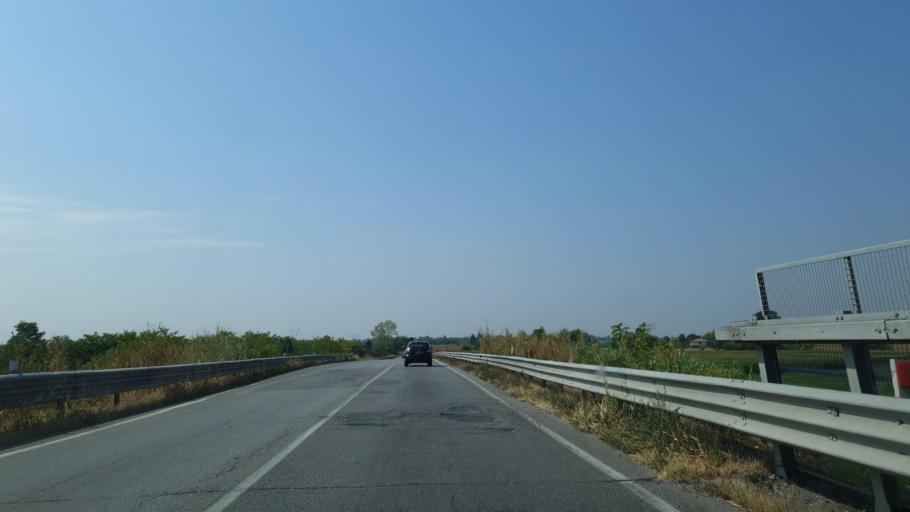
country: IT
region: Lombardy
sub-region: Provincia di Brescia
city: Leno
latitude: 45.3781
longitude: 10.2127
